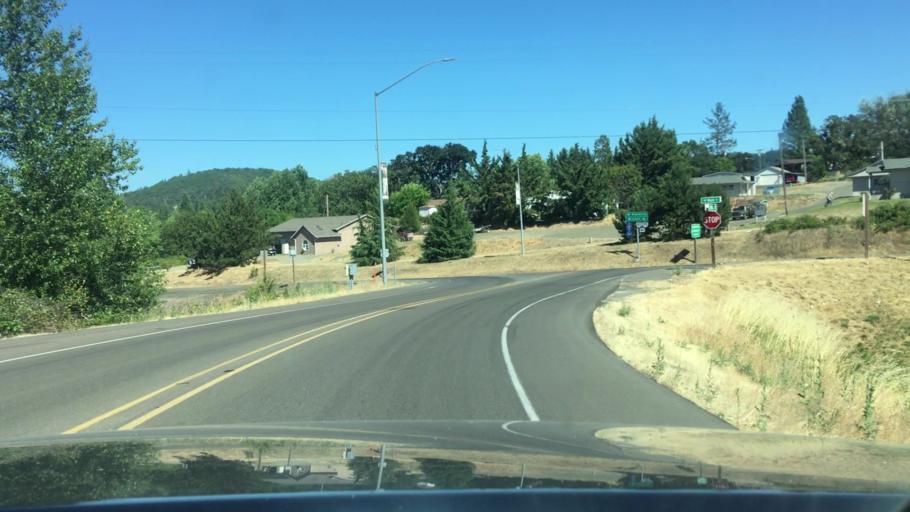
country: US
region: Oregon
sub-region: Douglas County
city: Winston
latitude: 43.1289
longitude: -123.4091
